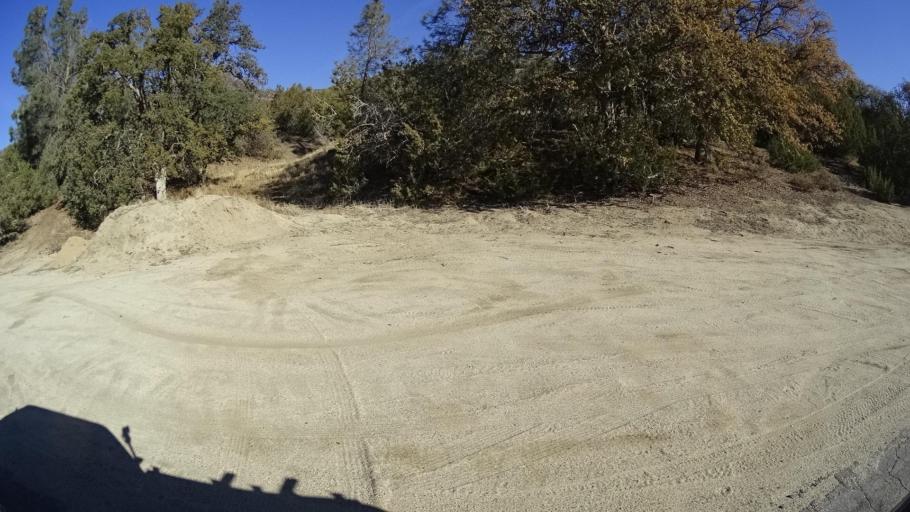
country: US
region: California
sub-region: Kern County
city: Bodfish
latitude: 35.3970
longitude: -118.4415
